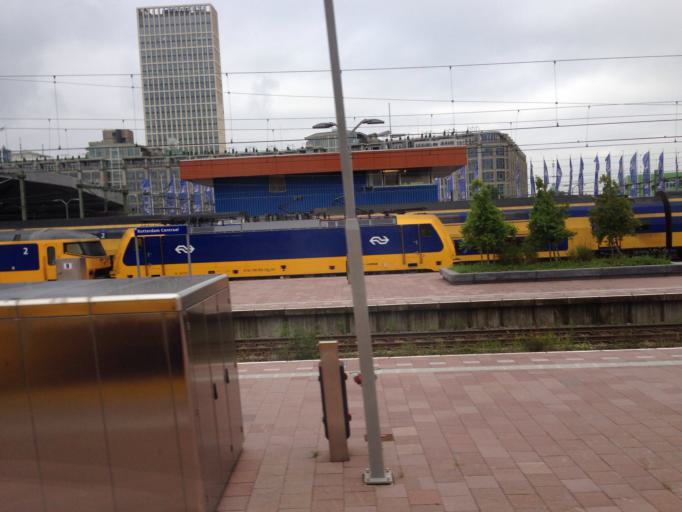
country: NL
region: South Holland
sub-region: Gemeente Rotterdam
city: Rotterdam
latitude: 51.9250
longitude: 4.4663
